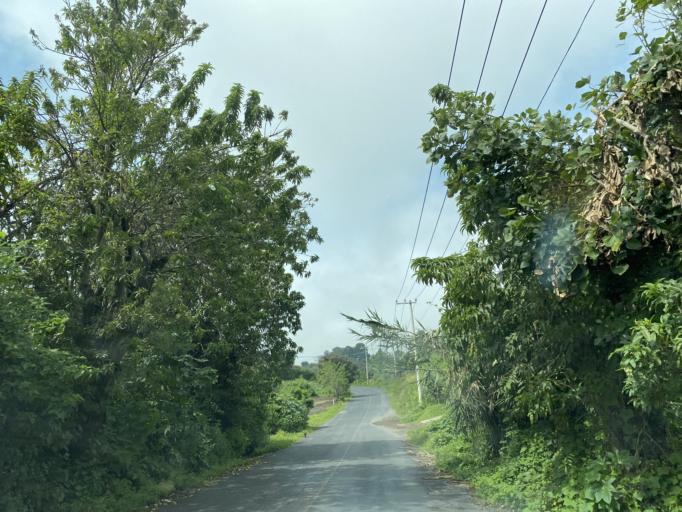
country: MX
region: Mexico
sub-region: Ozumba
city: San Jose Tlacotitlan
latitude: 18.9999
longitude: -98.8000
